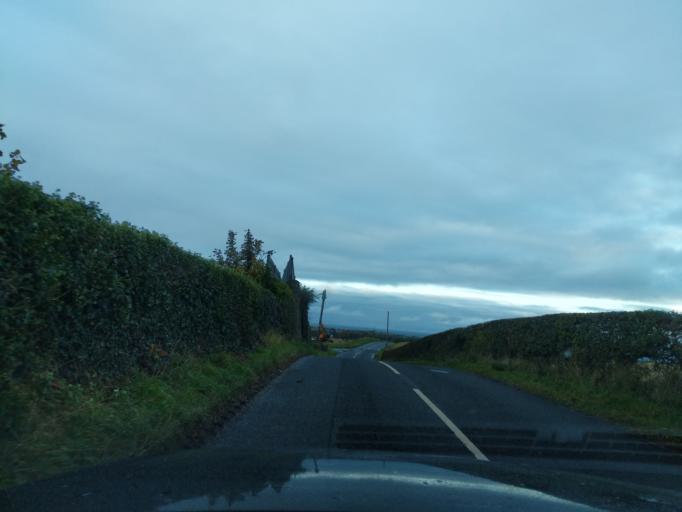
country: GB
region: Scotland
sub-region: East Lothian
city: Dunbar
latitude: 55.9794
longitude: -2.5185
